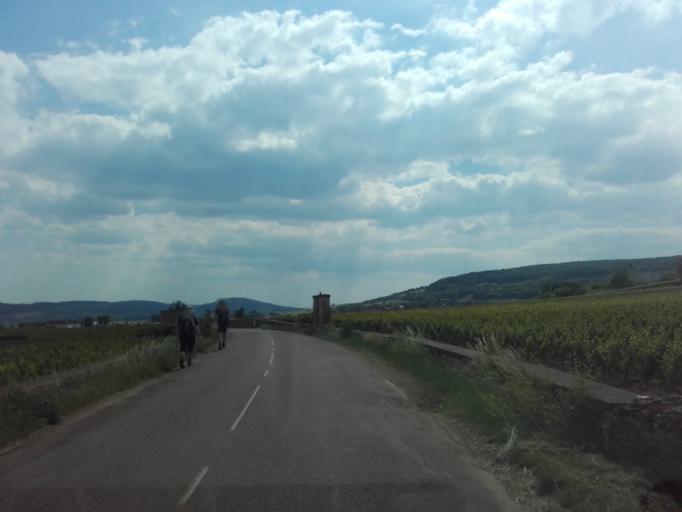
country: FR
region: Bourgogne
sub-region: Departement de la Cote-d'Or
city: Corpeau
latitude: 46.9449
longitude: 4.7390
